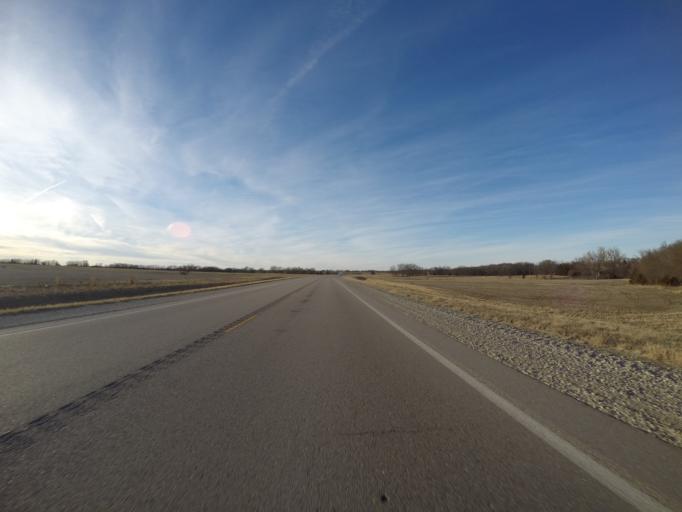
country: US
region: Kansas
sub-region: Marion County
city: Marion
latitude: 38.2545
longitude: -96.9538
